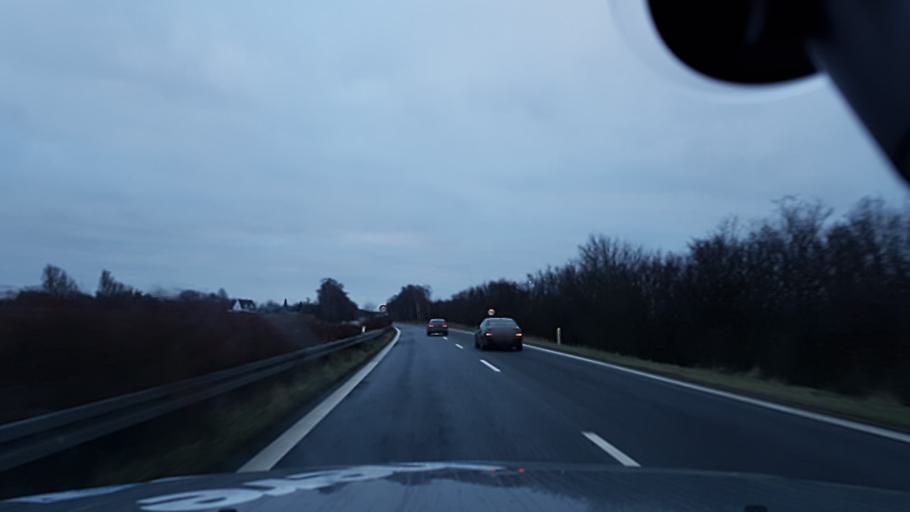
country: DK
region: Zealand
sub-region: Lolland Kommune
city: Maribo
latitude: 54.7670
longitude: 11.4623
